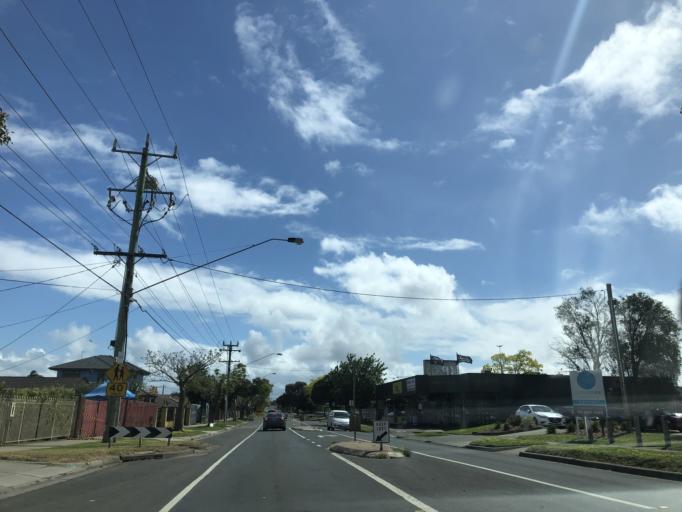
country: AU
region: Victoria
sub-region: Kingston
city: Clayton South
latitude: -37.9415
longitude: 145.1047
